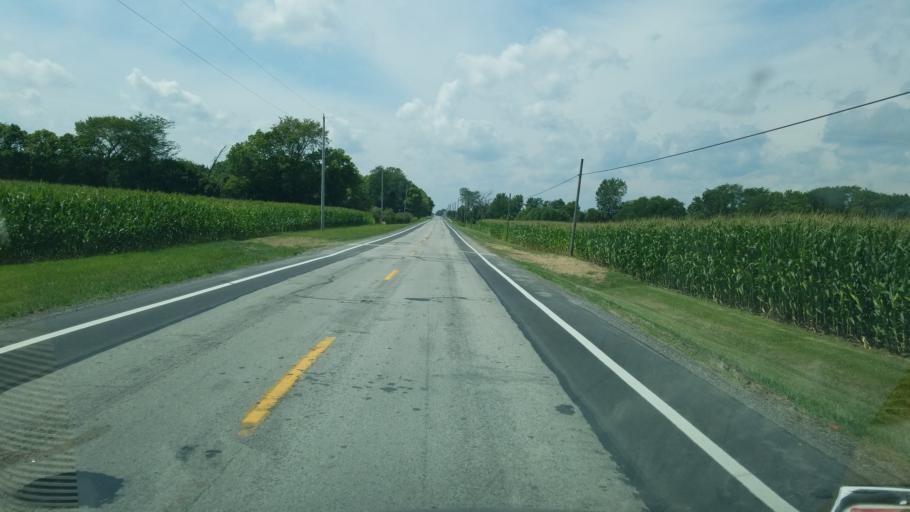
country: US
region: Ohio
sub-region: Hancock County
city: Arlington
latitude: 40.8924
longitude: -83.6755
